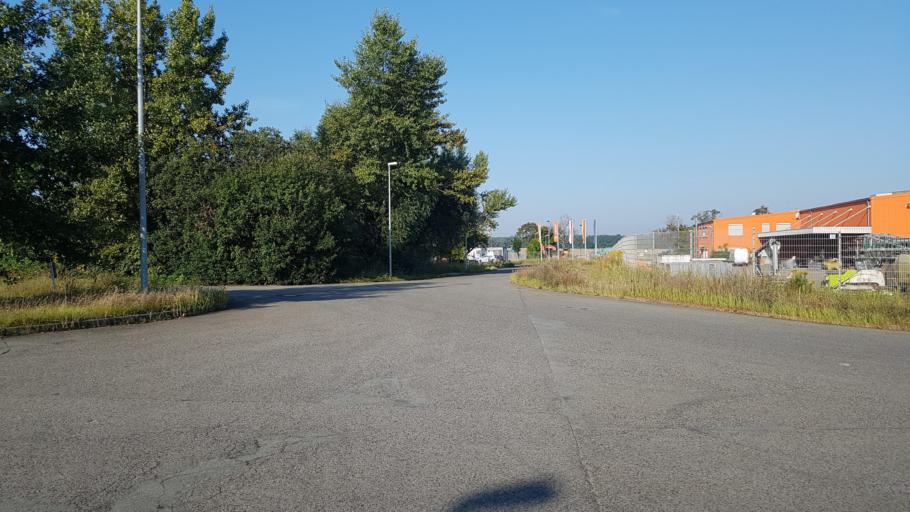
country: DE
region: Brandenburg
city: Brandenburg an der Havel
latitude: 52.3764
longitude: 12.5982
